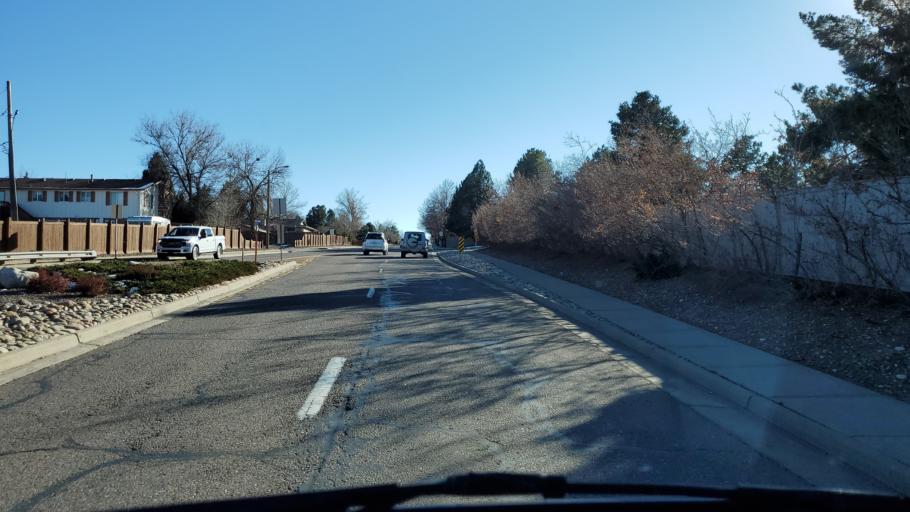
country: US
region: Colorado
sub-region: Arapahoe County
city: Castlewood
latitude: 39.5890
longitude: -104.9043
